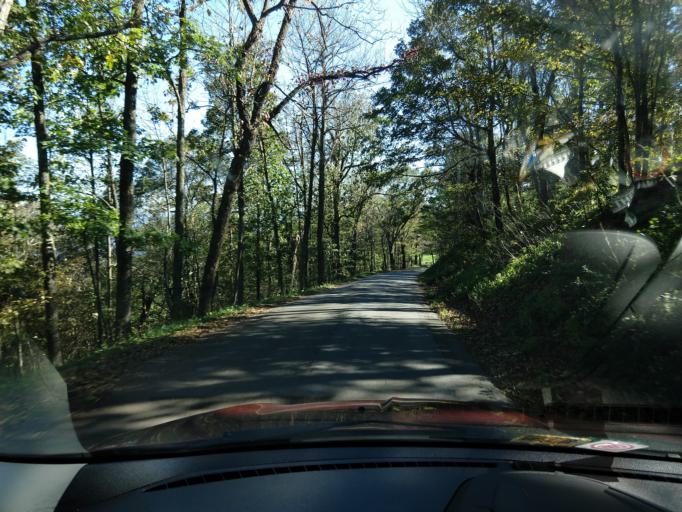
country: US
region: Virginia
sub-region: Alleghany County
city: Clifton Forge
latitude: 37.8732
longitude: -79.8870
